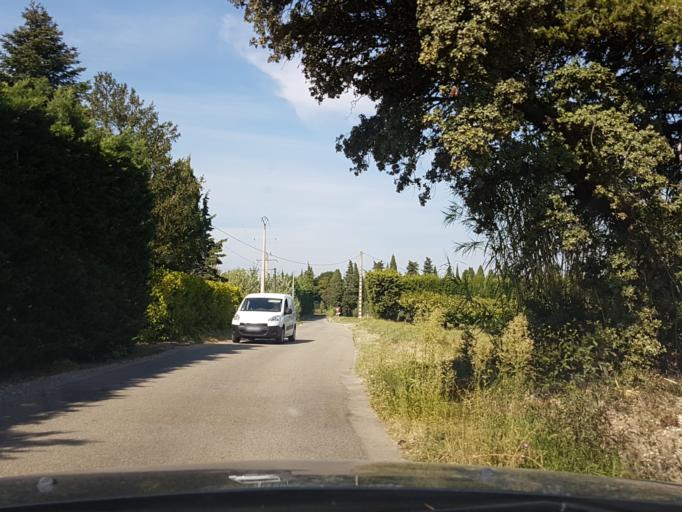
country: FR
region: Provence-Alpes-Cote d'Azur
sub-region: Departement des Bouches-du-Rhone
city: Eygalieres
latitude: 43.7828
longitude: 4.9230
